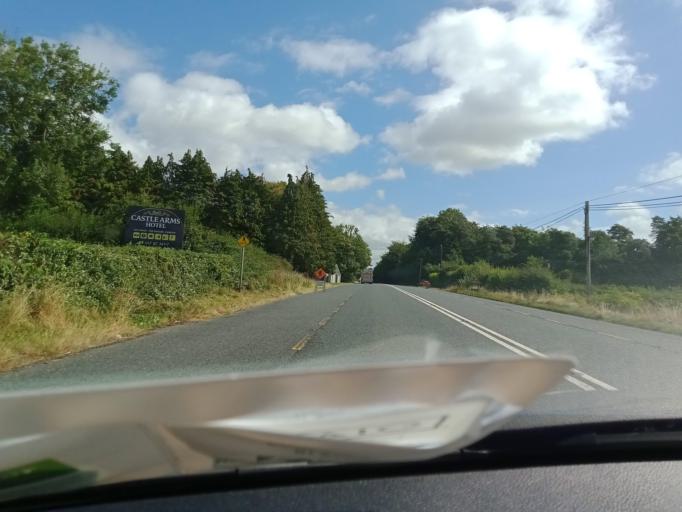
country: IE
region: Leinster
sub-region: Laois
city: Abbeyleix
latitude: 52.8374
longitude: -7.4298
